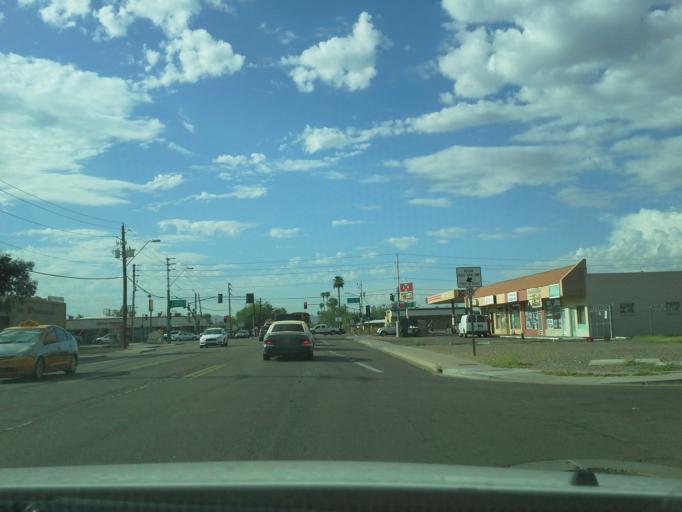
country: US
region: Arizona
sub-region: Maricopa County
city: Phoenix
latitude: 33.4961
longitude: -112.0914
